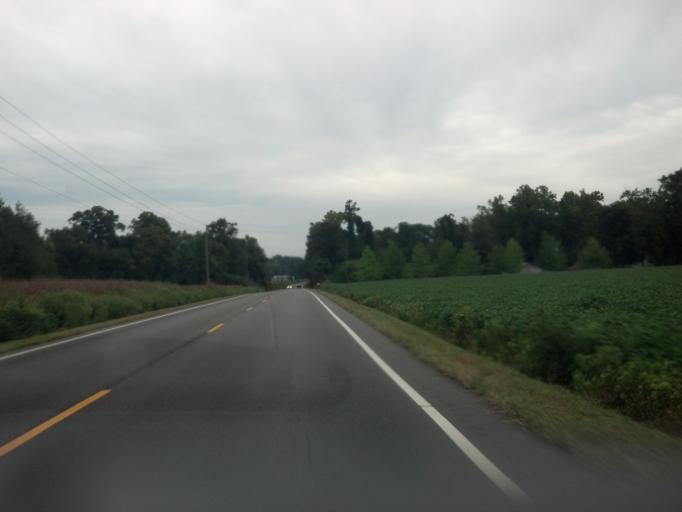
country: US
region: North Carolina
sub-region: Pitt County
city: Ayden
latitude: 35.4638
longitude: -77.4820
